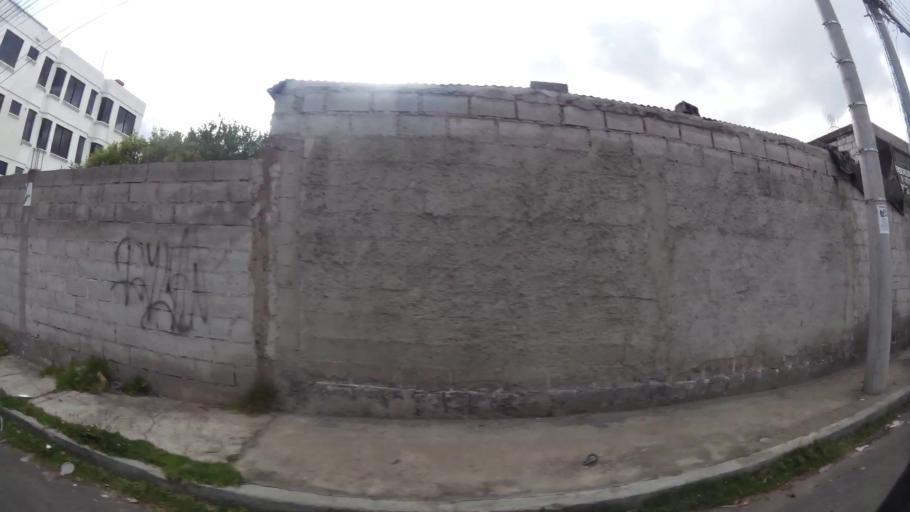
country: EC
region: Pichincha
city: Quito
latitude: -0.1347
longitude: -78.4637
